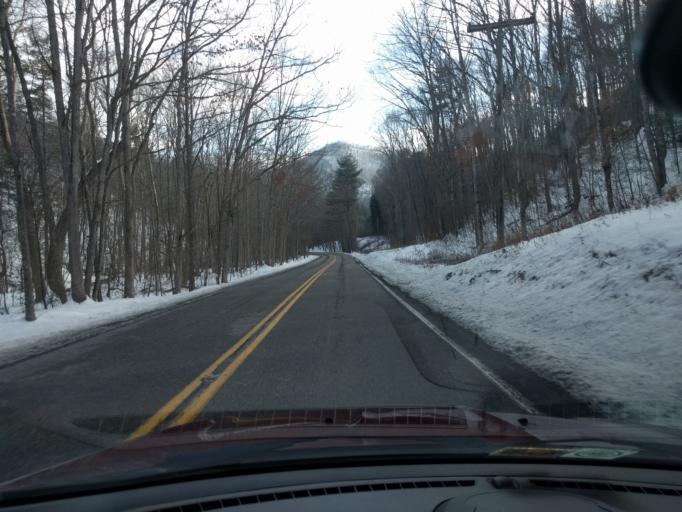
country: US
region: Virginia
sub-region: Bath County
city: Warm Springs
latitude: 38.1243
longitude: -79.9277
